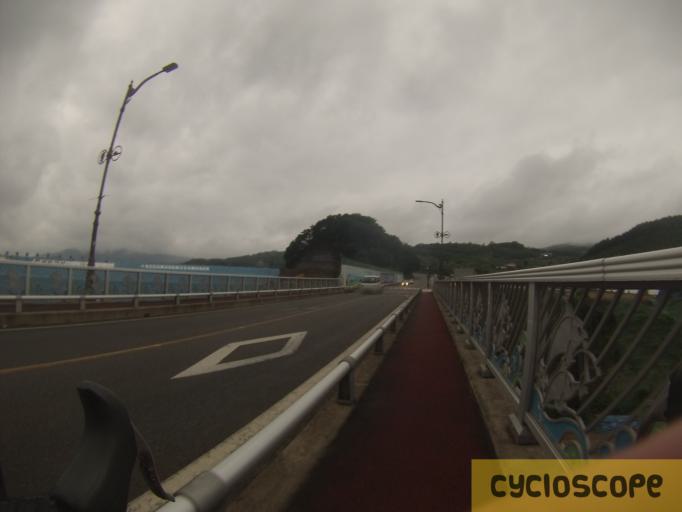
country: KR
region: Chungcheongnam-do
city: Yesan
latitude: 36.7497
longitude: 126.8867
